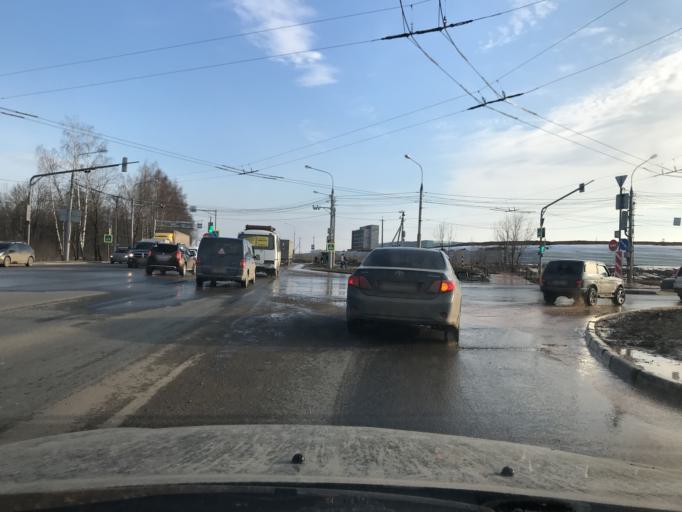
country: RU
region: Kaluga
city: Kaluga
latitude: 54.4935
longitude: 36.2282
